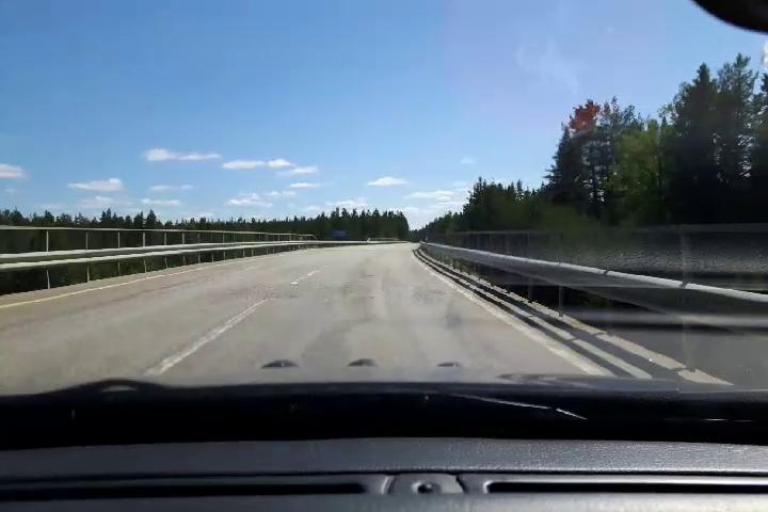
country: SE
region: Jaemtland
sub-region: Harjedalens Kommun
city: Sveg
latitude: 62.1233
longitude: 15.0349
